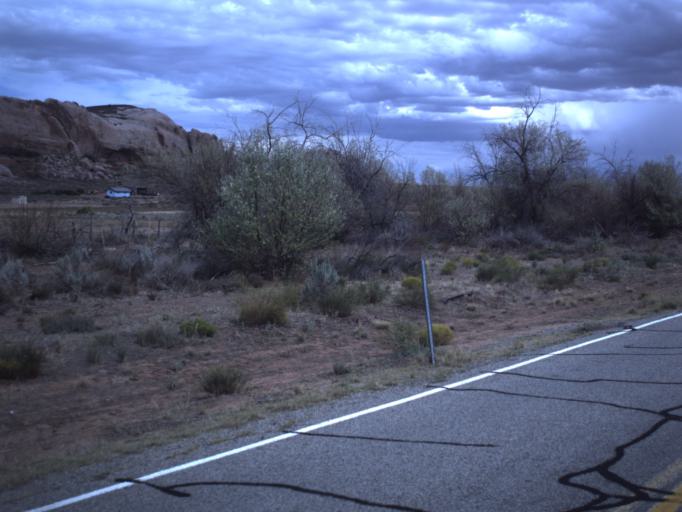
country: US
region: Utah
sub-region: San Juan County
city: Blanding
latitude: 37.2826
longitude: -109.5129
